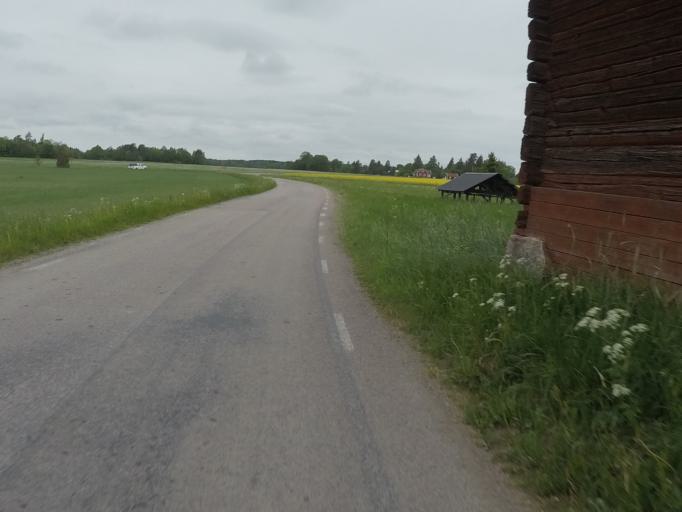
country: SE
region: Vaestmanland
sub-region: Hallstahammars Kommun
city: Kolback
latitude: 59.5475
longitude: 16.2938
